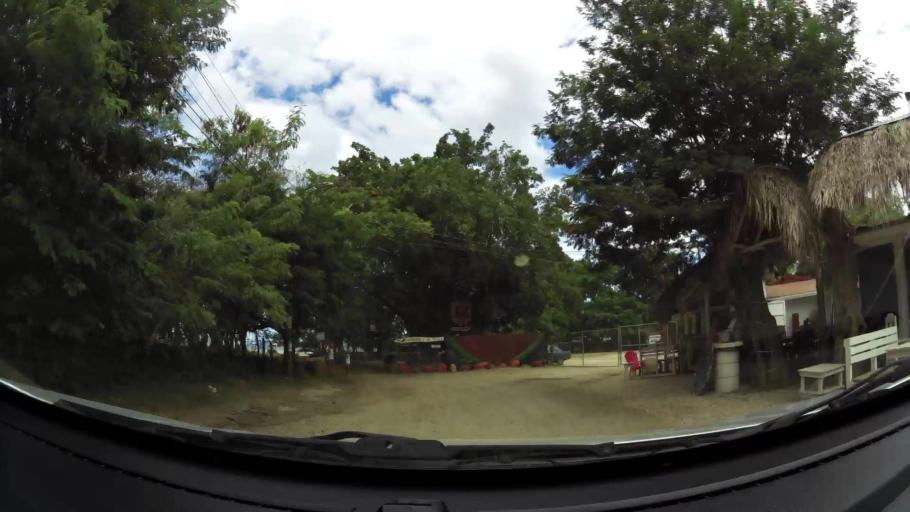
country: CR
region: Guanacaste
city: Santa Cruz
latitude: 10.2973
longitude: -85.8429
